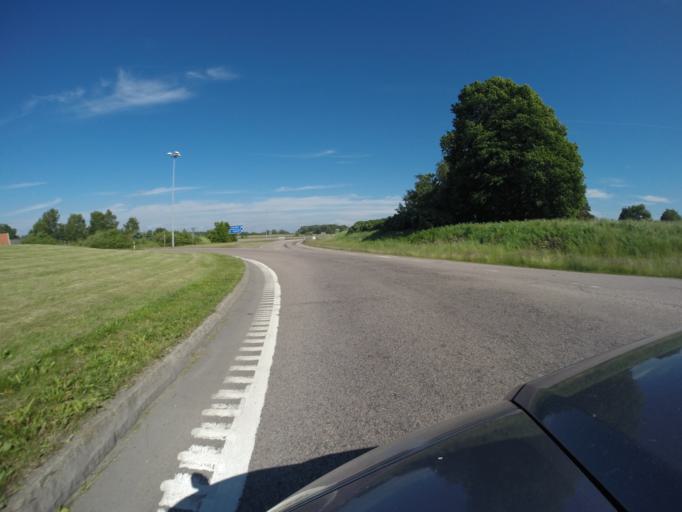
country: SE
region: Skane
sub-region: Bjuvs Kommun
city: Billesholm
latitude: 56.0107
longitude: 12.9562
